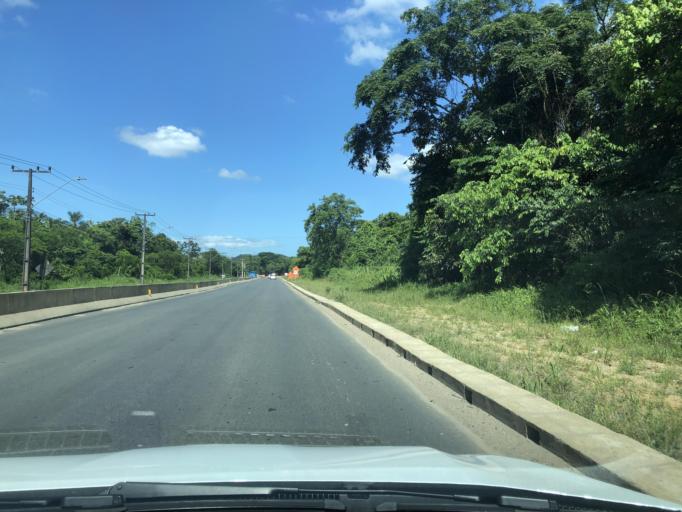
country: BR
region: Santa Catarina
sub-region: Joinville
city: Joinville
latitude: -26.2501
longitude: -48.8608
